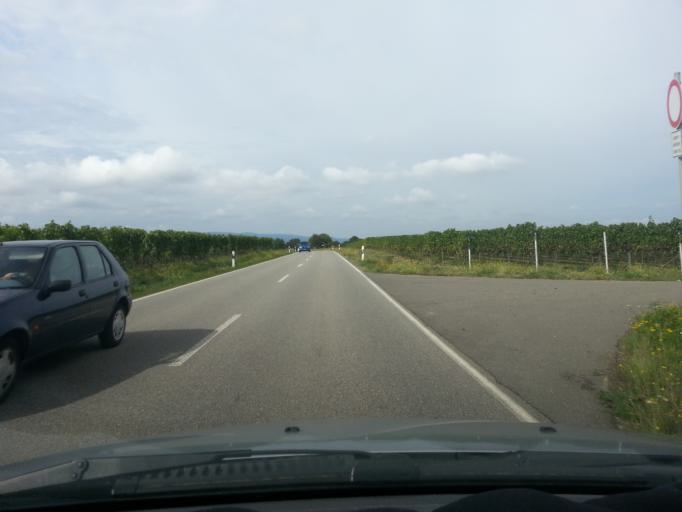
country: DE
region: Rheinland-Pfalz
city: Lachen-Speyerdorf
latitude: 49.3069
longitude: 8.2010
